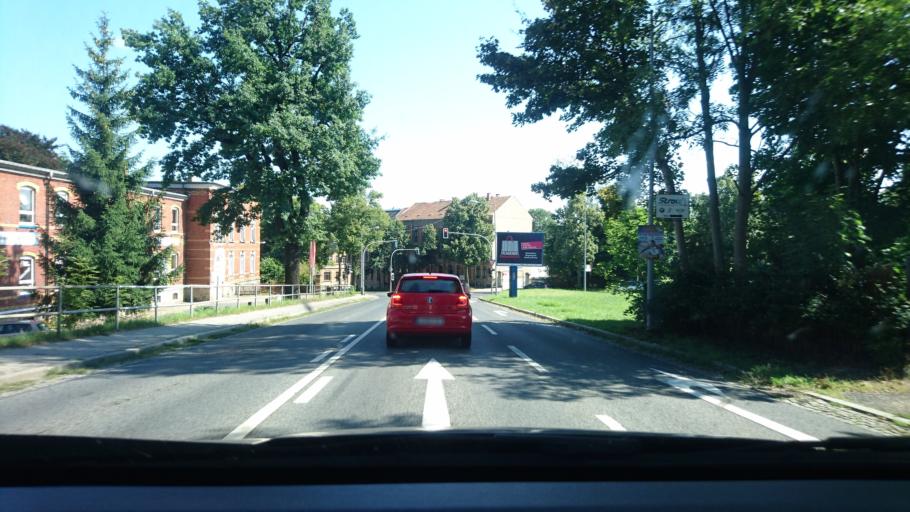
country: DE
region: Saxony
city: Auerbach
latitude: 50.5149
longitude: 12.3927
